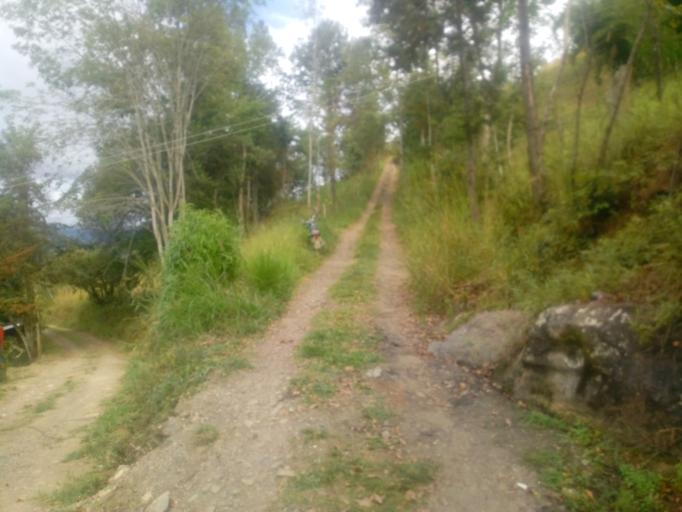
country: CO
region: Cundinamarca
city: Tenza
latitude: 5.0734
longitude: -73.4216
